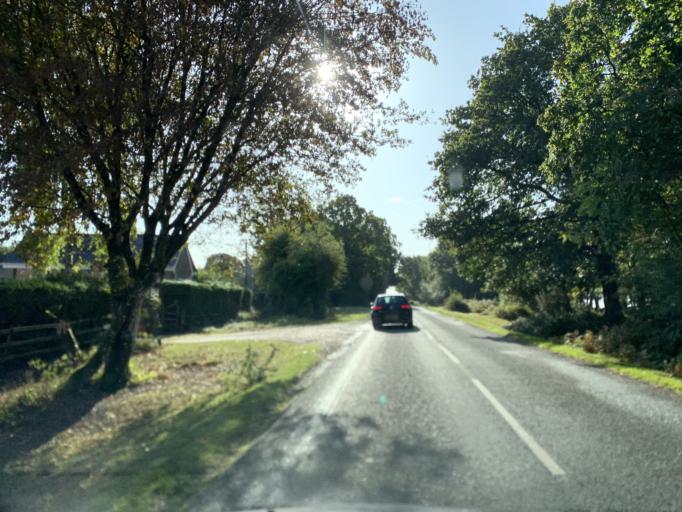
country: GB
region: England
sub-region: Wiltshire
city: Downton
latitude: 50.9628
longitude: -1.7012
